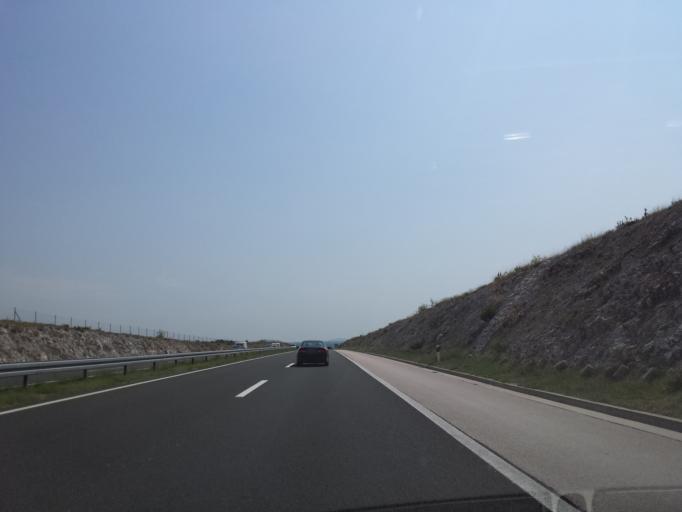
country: HR
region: Zadarska
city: Polaca
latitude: 44.0749
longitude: 15.5148
